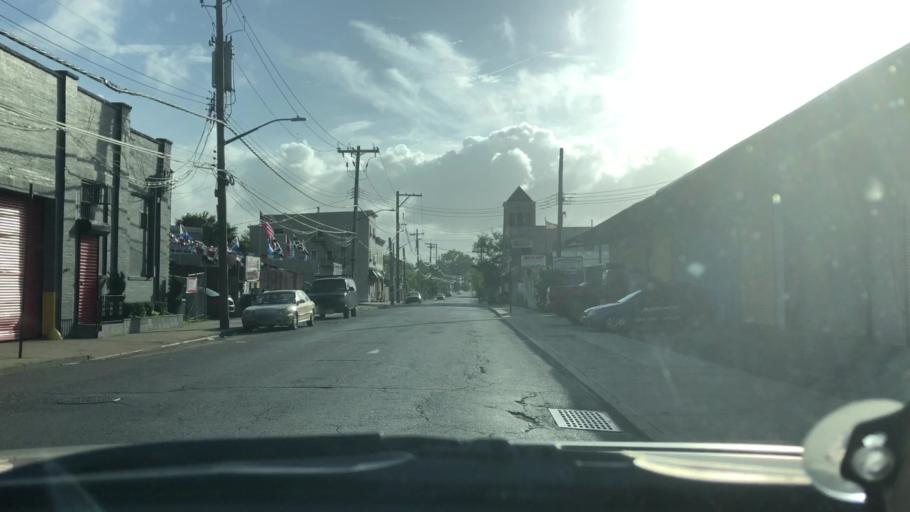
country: US
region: New York
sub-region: Richmond County
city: Bloomfield
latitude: 40.6377
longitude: -74.1462
